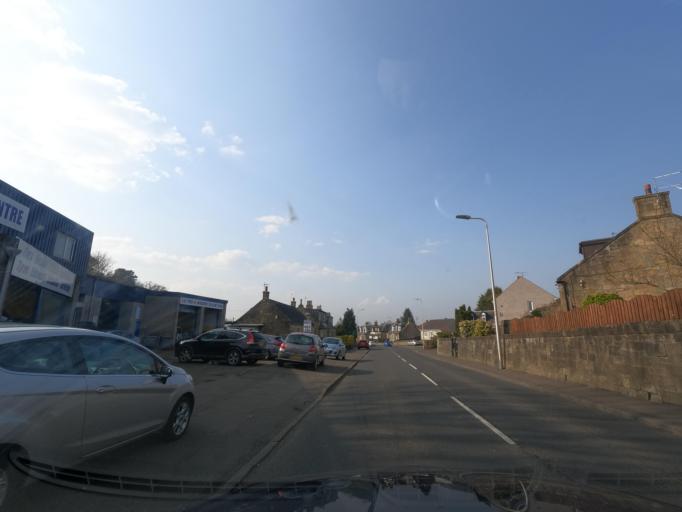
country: GB
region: Scotland
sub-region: Falkirk
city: Grangemouth
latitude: 55.9873
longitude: -3.7394
